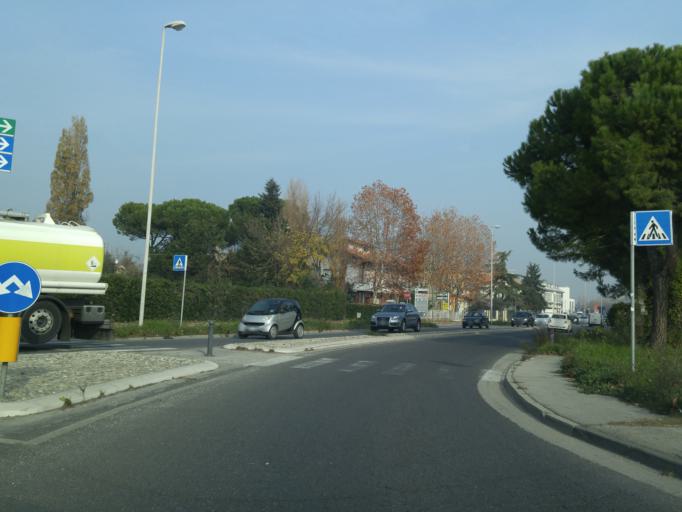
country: IT
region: Emilia-Romagna
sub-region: Provincia di Rimini
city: Montalbano
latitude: 43.9478
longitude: 12.7217
